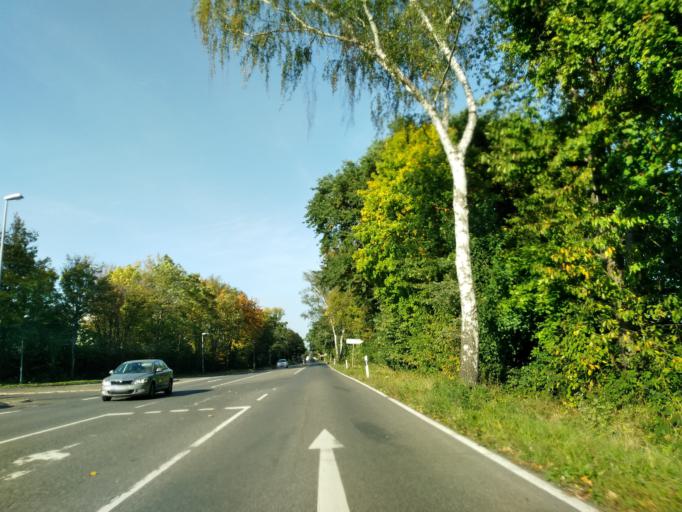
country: DE
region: North Rhine-Westphalia
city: Sankt Augustin
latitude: 50.7652
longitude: 7.2151
